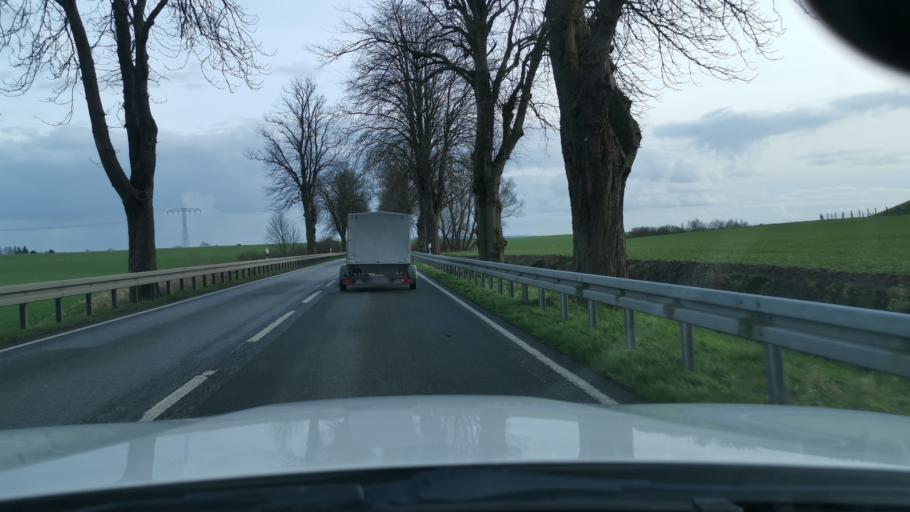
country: DE
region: Mecklenburg-Vorpommern
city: Laage
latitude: 53.9474
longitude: 12.3079
